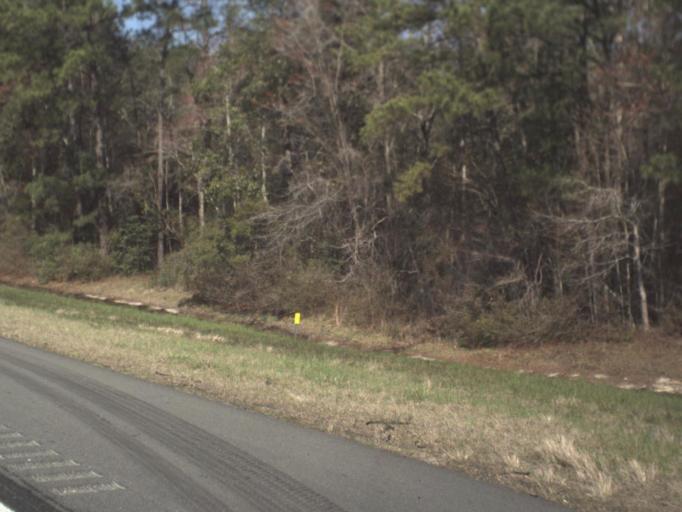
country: US
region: Florida
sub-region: Gadsden County
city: Chattahoochee
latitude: 30.6225
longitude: -84.7984
